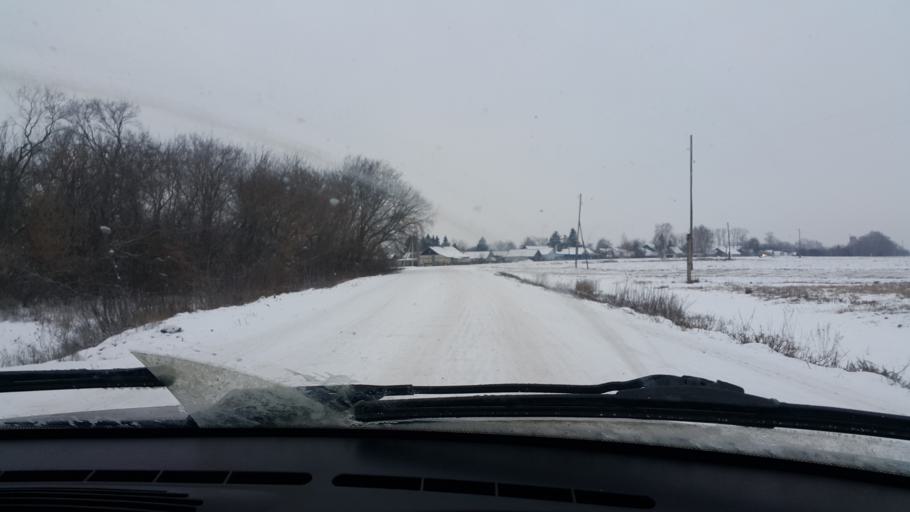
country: RU
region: Tambov
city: Inzhavino
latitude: 52.4697
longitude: 42.3914
